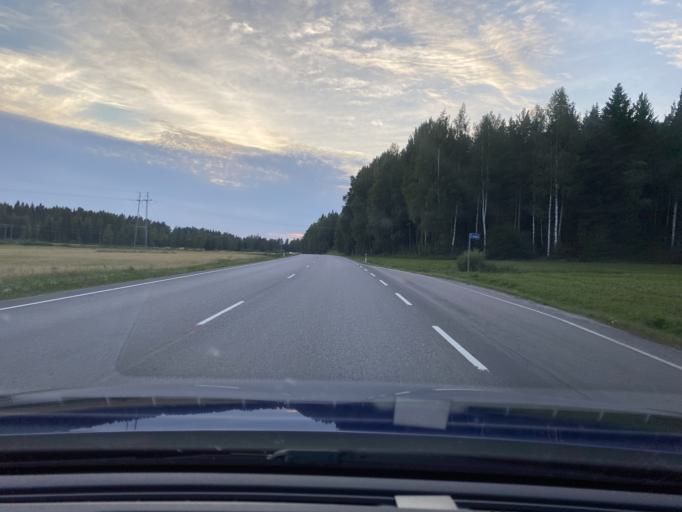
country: FI
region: Satakunta
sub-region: Pohjois-Satakunta
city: Kankaanpaeae
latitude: 61.7789
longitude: 22.4476
